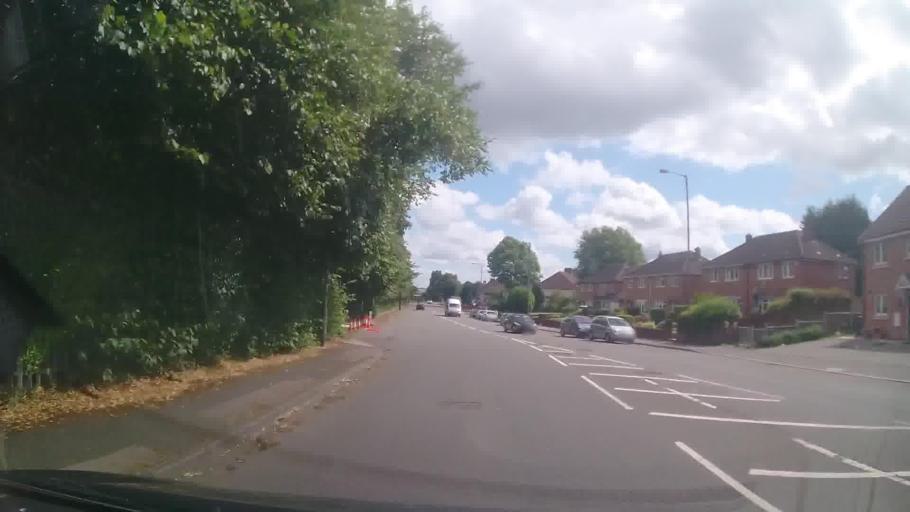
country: GB
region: England
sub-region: Walsall
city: Darlaston
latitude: 52.5700
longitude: -2.0181
